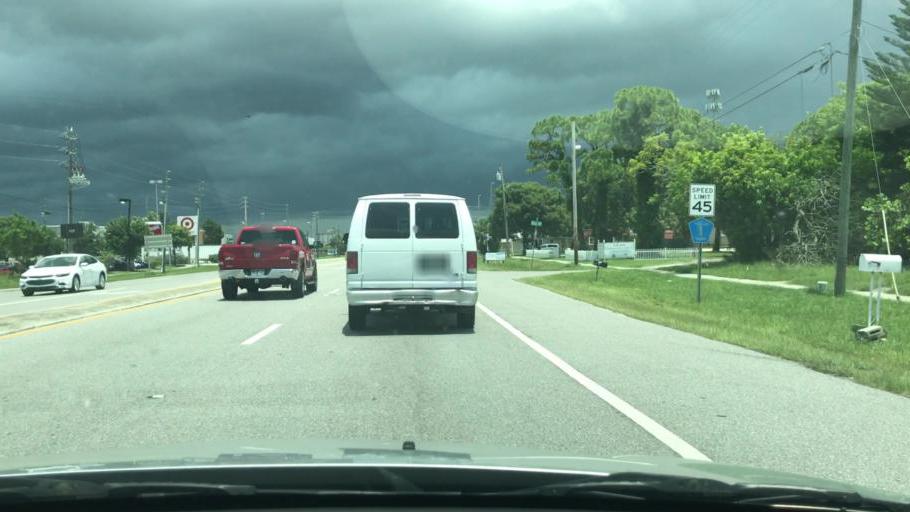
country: US
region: Florida
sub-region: Pinellas County
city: Bay Pines
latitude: 27.8117
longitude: -82.7538
